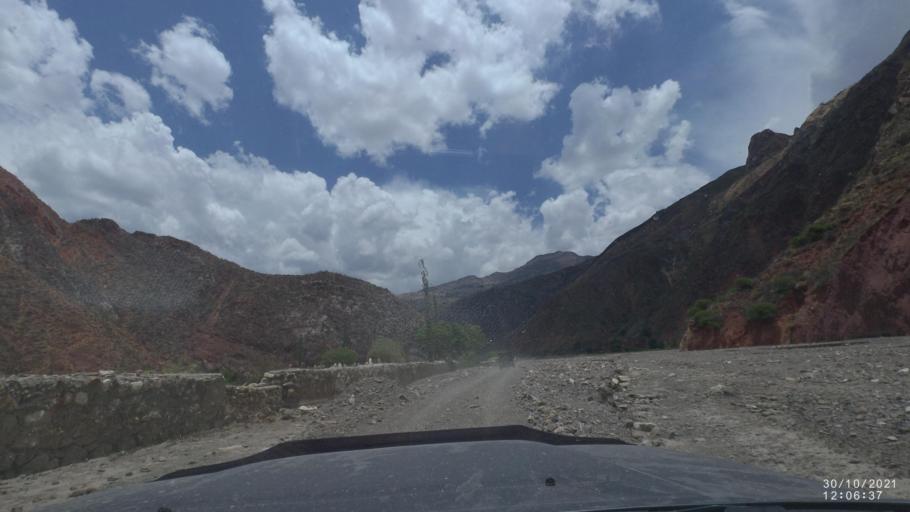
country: BO
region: Cochabamba
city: Colchani
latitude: -17.5367
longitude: -66.6235
